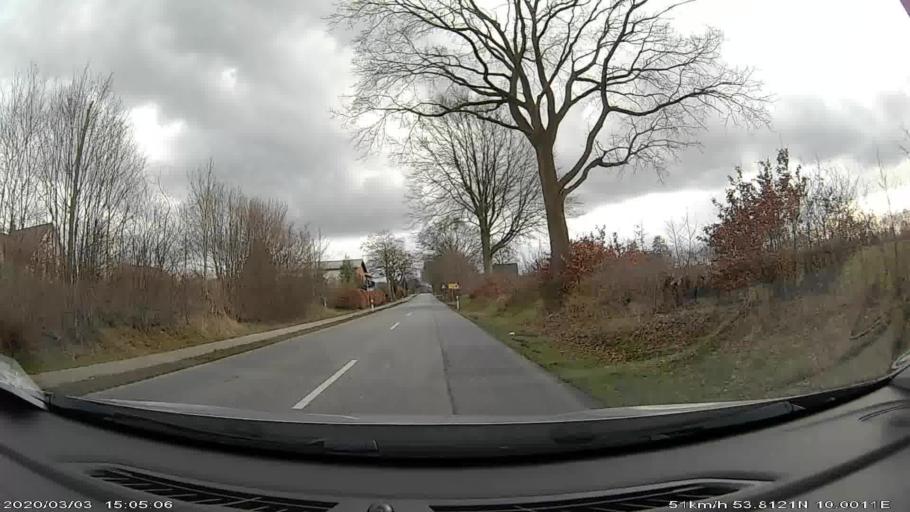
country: DE
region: Schleswig-Holstein
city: Kisdorf
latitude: 53.8124
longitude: 10.0010
